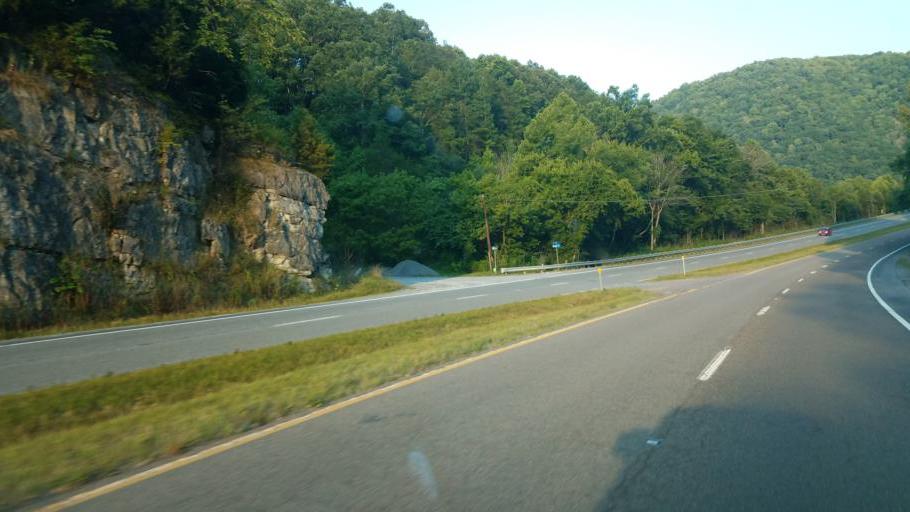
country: US
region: Tennessee
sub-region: Hawkins County
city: Mount Carmel
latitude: 36.6971
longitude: -82.7571
